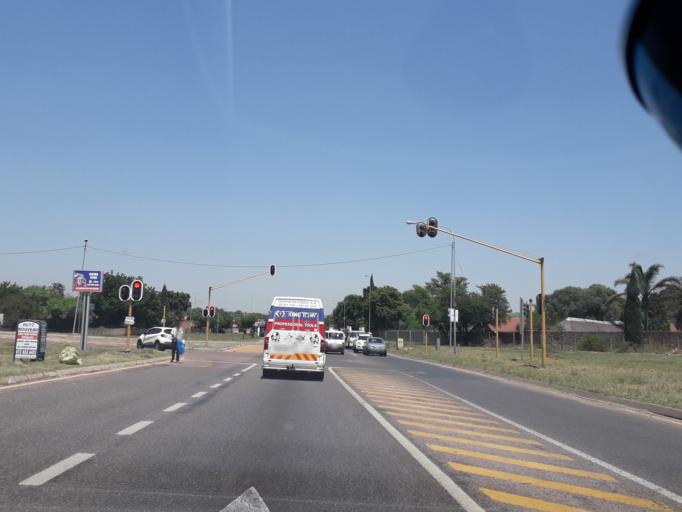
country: ZA
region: Gauteng
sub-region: City of Tshwane Metropolitan Municipality
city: Centurion
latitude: -25.8707
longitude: 28.1767
